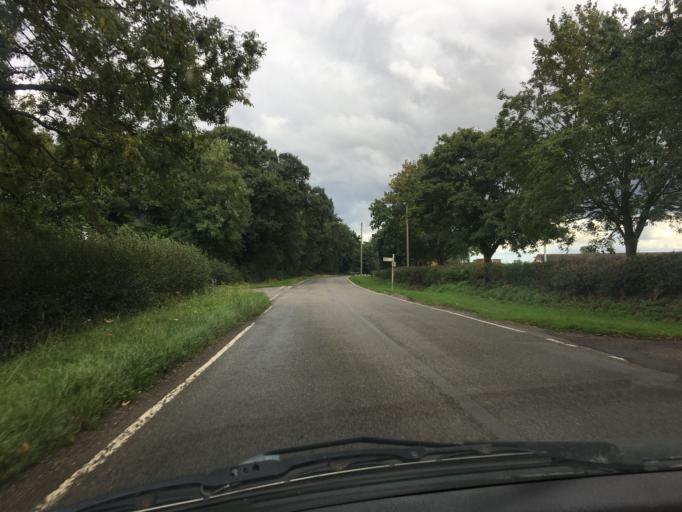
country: GB
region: England
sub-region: Leicestershire
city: Lutterworth
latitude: 52.4839
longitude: -1.2180
